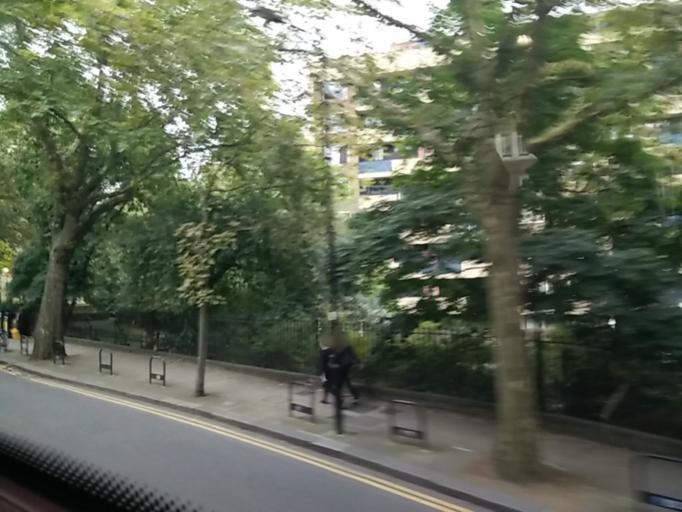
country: GB
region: England
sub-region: Greater London
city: Clerkenwell
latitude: 51.5287
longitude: -0.1066
